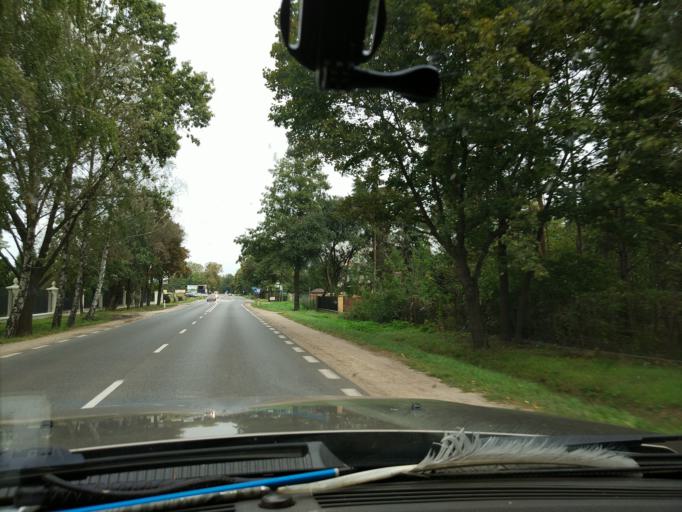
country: PL
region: Masovian Voivodeship
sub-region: Powiat pruszkowski
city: Otrebusy
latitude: 52.1333
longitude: 20.7613
